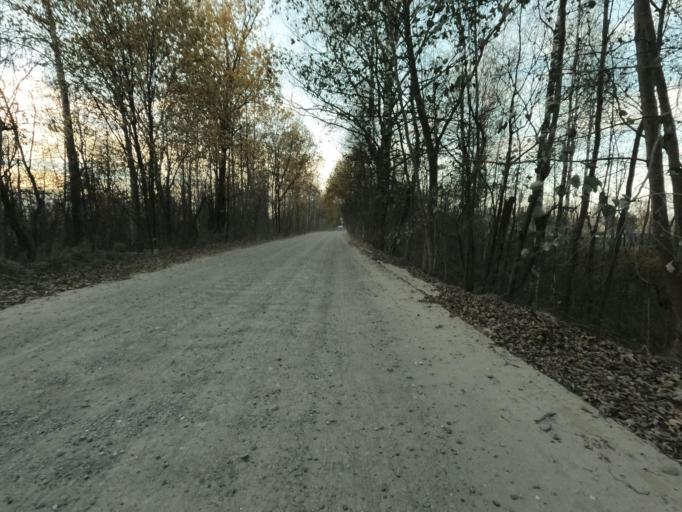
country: RU
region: Leningrad
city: Mga
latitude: 59.7695
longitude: 31.2316
